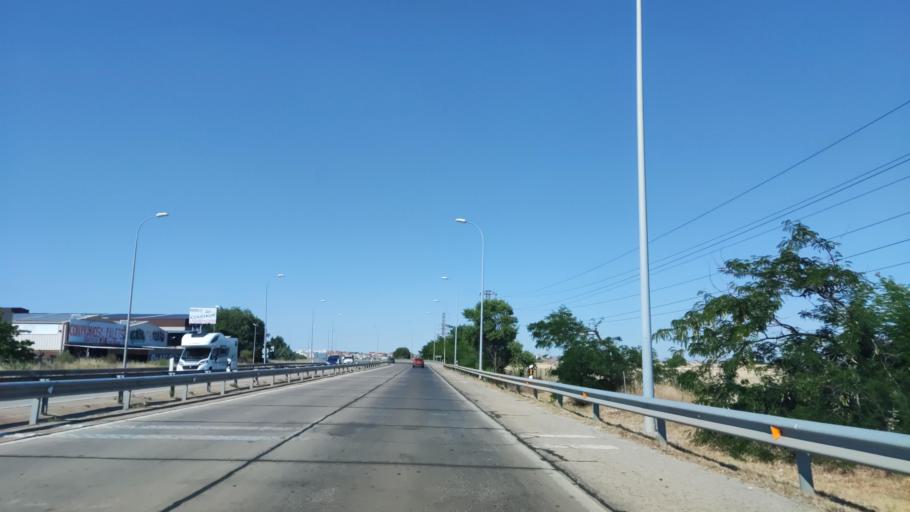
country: ES
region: Madrid
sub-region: Provincia de Madrid
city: Alcorcon
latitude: 40.3466
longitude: -3.7961
